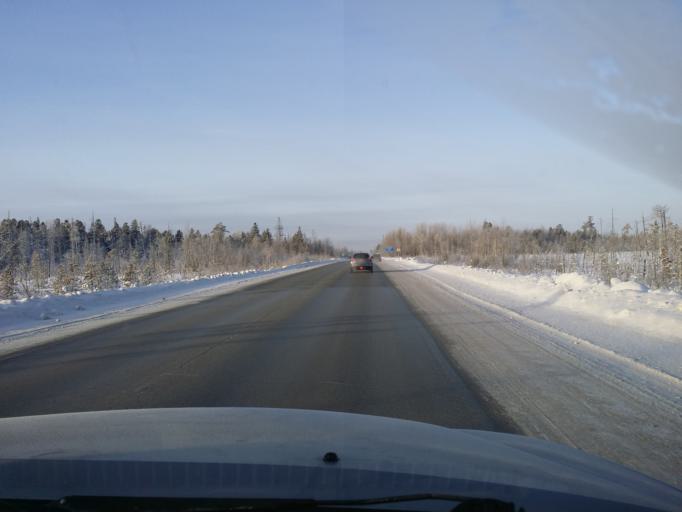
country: RU
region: Khanty-Mansiyskiy Avtonomnyy Okrug
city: Langepas
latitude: 61.2414
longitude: 75.2749
